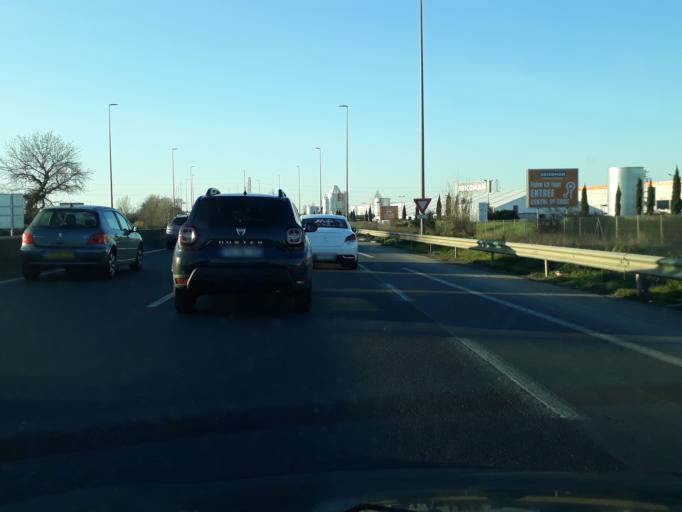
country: FR
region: Midi-Pyrenees
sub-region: Departement de la Haute-Garonne
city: Portet-sur-Garonne
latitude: 43.5512
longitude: 1.4154
